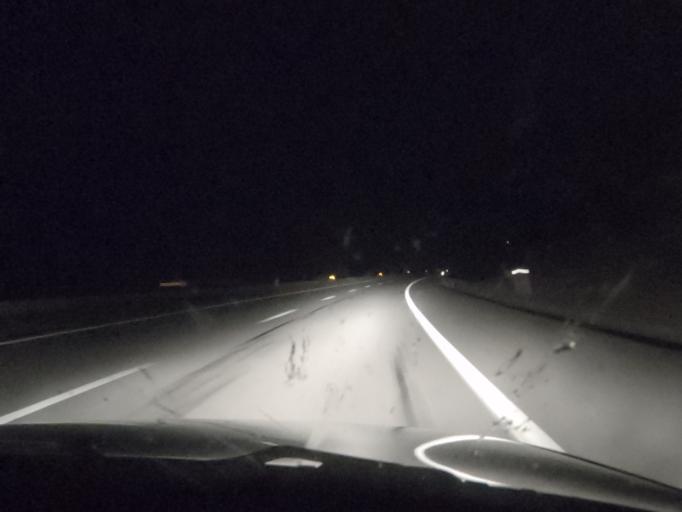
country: PT
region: Evora
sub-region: Estremoz
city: Estremoz
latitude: 38.8278
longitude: -7.6109
